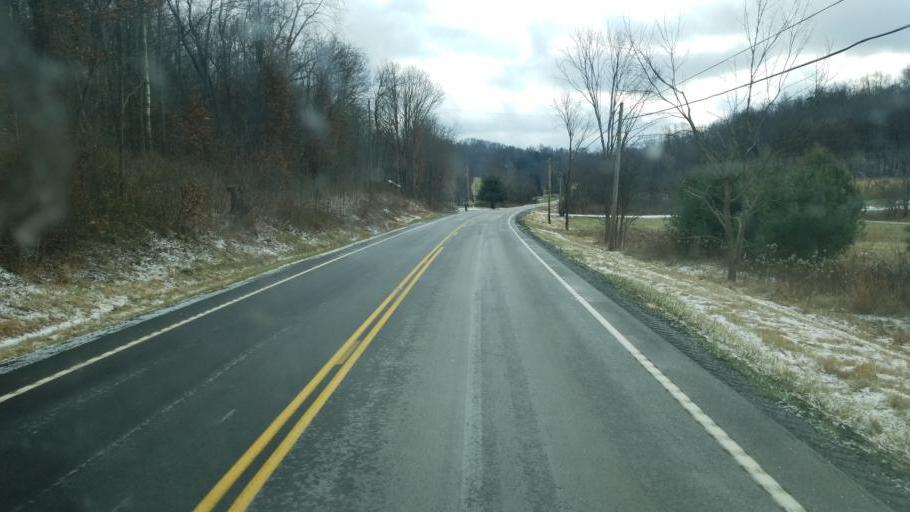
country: US
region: Ohio
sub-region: Muskingum County
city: Frazeysburg
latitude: 40.1248
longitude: -82.1921
